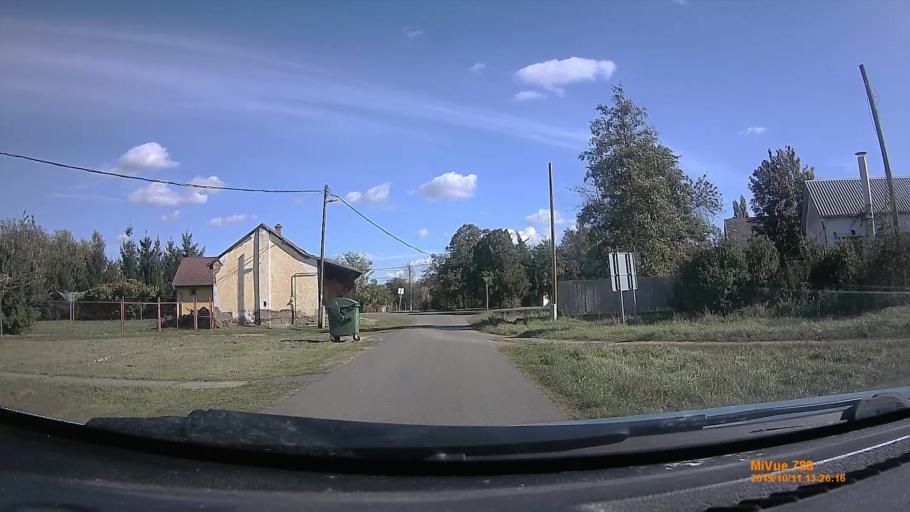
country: HU
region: Hajdu-Bihar
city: Balmazujvaros
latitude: 47.5394
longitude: 21.3138
